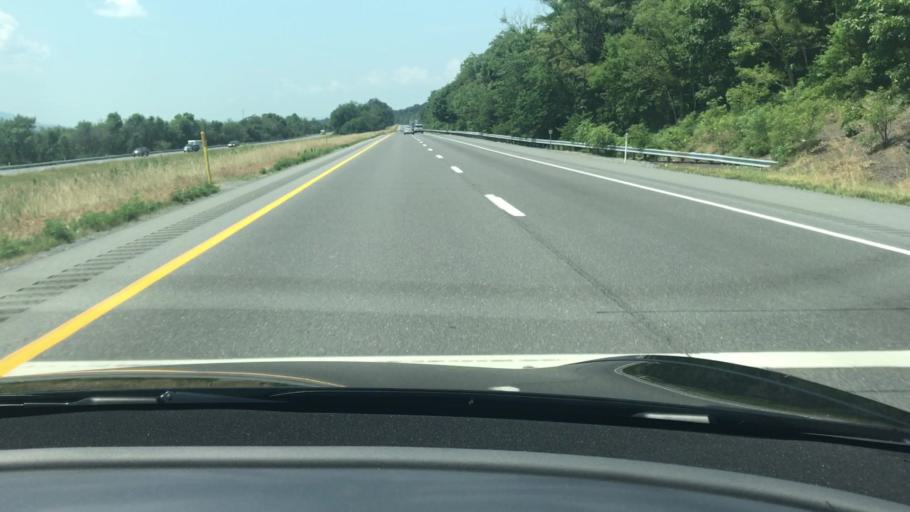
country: US
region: Pennsylvania
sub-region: Juniata County
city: Mifflintown
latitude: 40.5567
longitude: -77.2898
